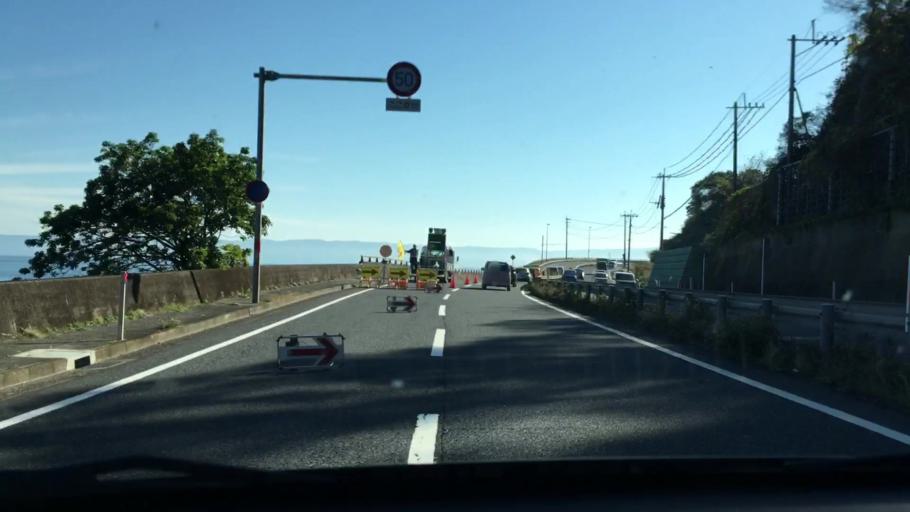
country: JP
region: Kagoshima
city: Kajiki
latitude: 31.6600
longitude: 130.6168
